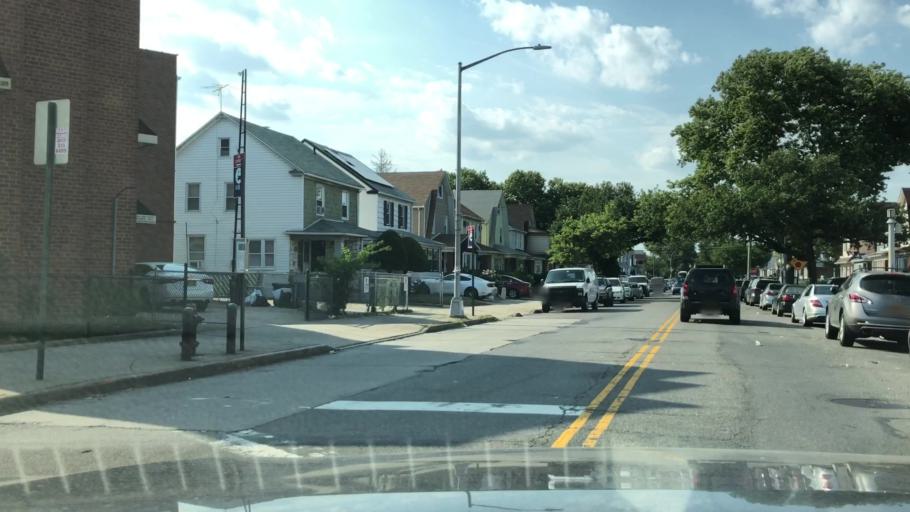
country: US
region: New York
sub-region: Queens County
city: Borough of Queens
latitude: 40.6777
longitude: -73.8276
